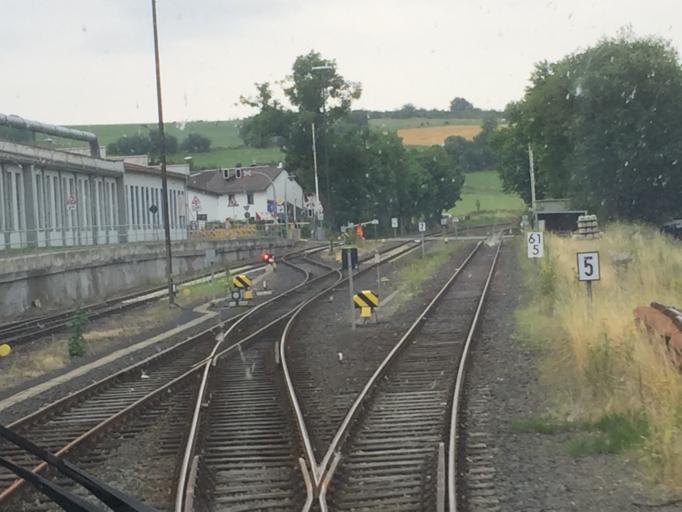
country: DE
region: Hesse
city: Frankenberg
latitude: 51.0517
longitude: 8.7863
